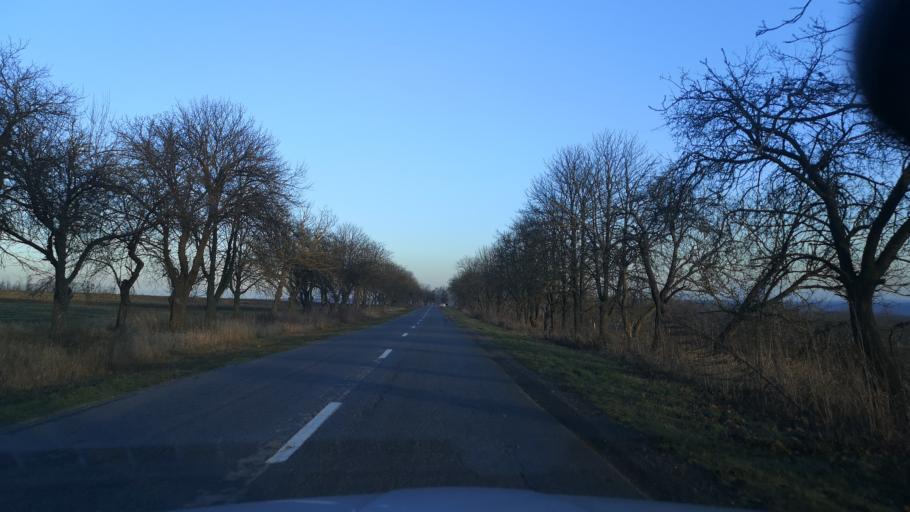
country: MD
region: Orhei
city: Orhei
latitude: 47.3120
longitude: 28.9550
